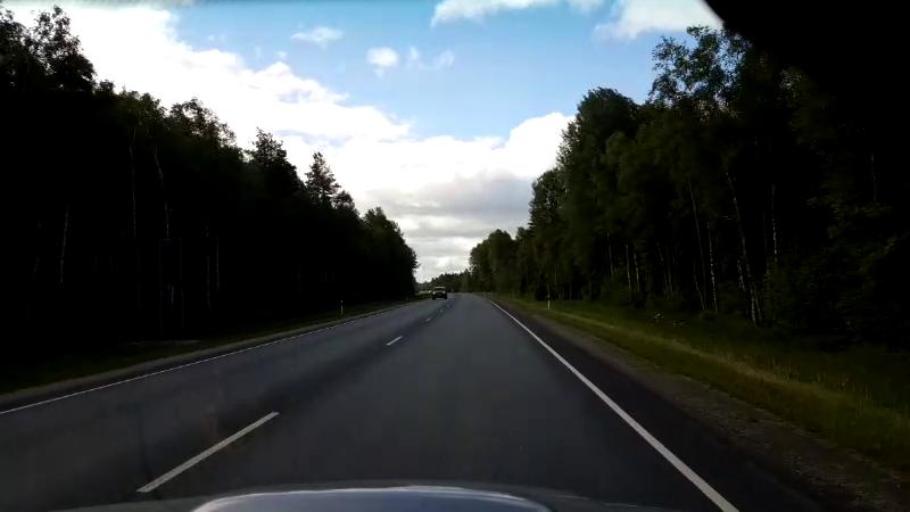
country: EE
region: Raplamaa
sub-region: Maerjamaa vald
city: Marjamaa
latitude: 59.0418
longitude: 24.4430
